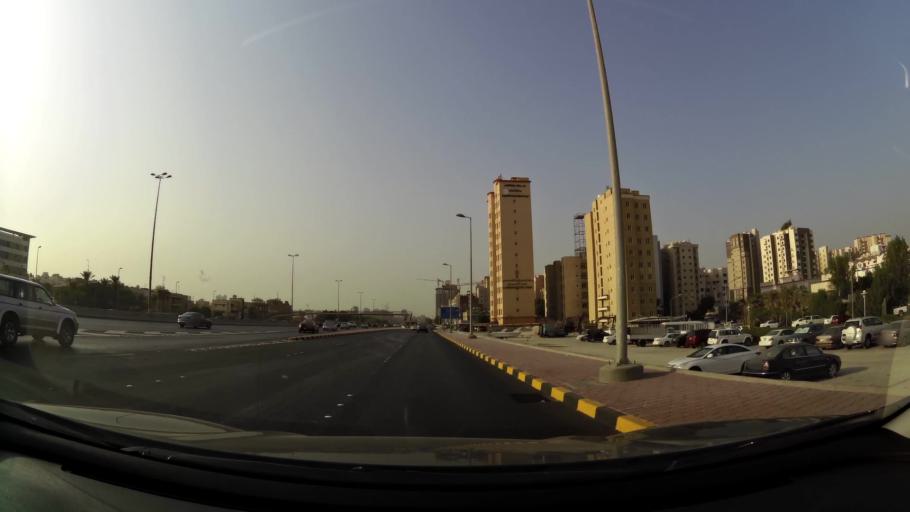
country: KW
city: Bayan
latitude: 29.3220
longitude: 48.0472
